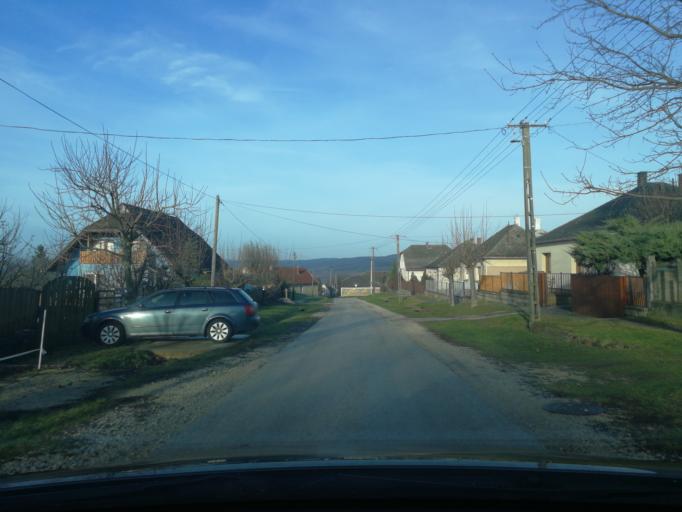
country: HU
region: Veszprem
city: Balatonfured
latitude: 47.0091
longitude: 17.7946
